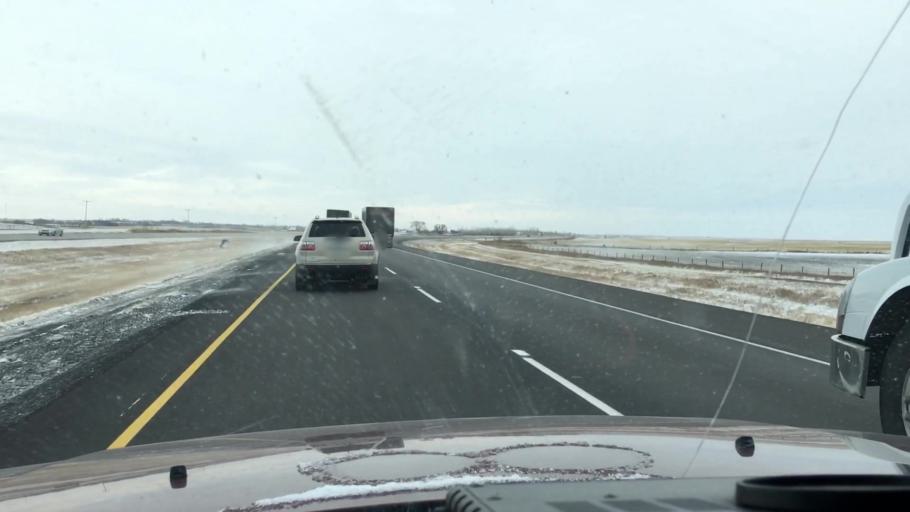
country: CA
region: Saskatchewan
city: Saskatoon
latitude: 51.7818
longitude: -106.4779
